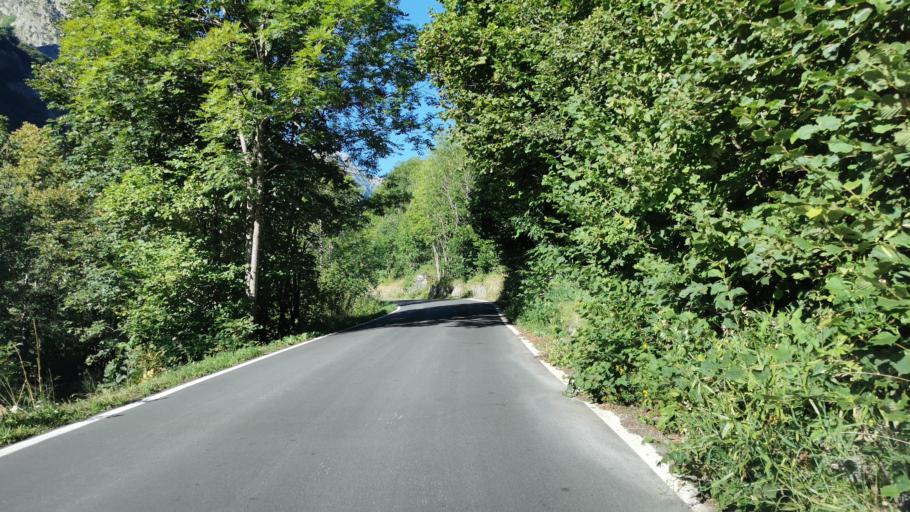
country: IT
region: Piedmont
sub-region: Provincia di Cuneo
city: Demonte
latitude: 44.2305
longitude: 7.3108
